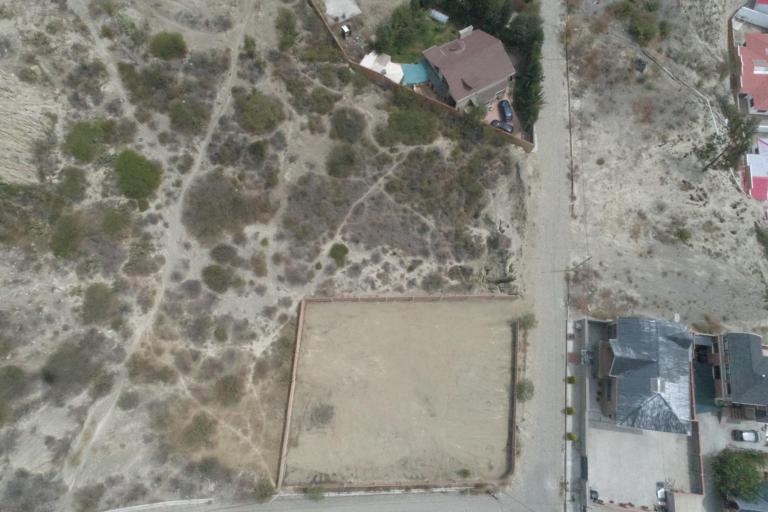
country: BO
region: La Paz
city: La Paz
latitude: -16.5987
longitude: -68.0697
